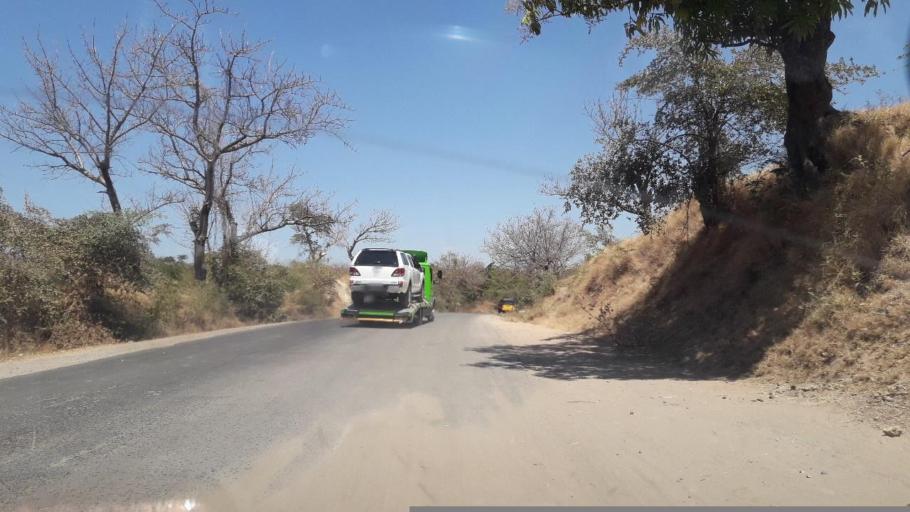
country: MG
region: Boeny
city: Ambato Boeny
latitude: -16.4951
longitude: 47.1531
